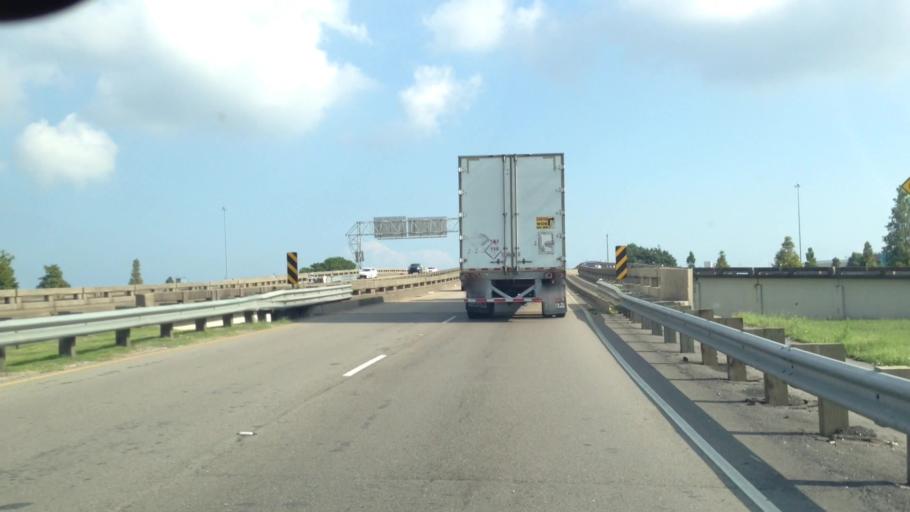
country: US
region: Louisiana
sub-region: Jefferson Parish
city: Metairie Terrace
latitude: 29.9969
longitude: -90.1838
